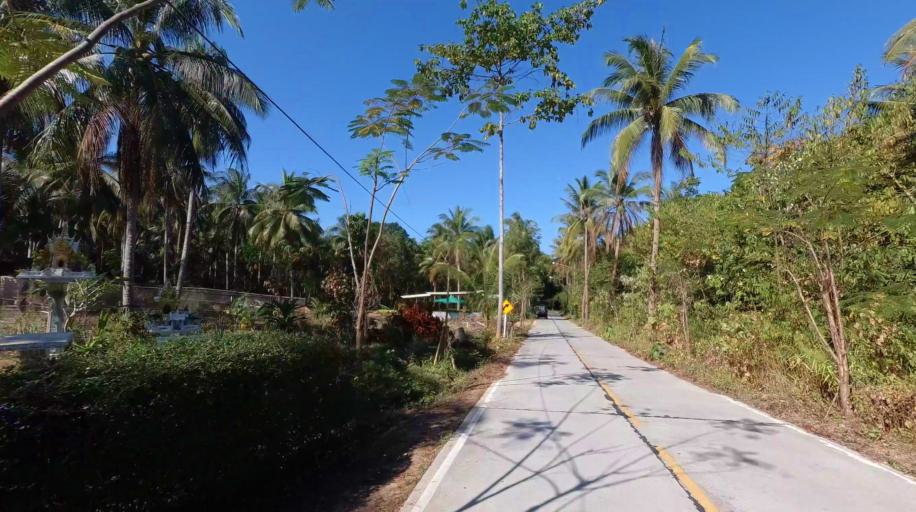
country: TH
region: Trat
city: Ko Kut
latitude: 11.6155
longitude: 102.5419
